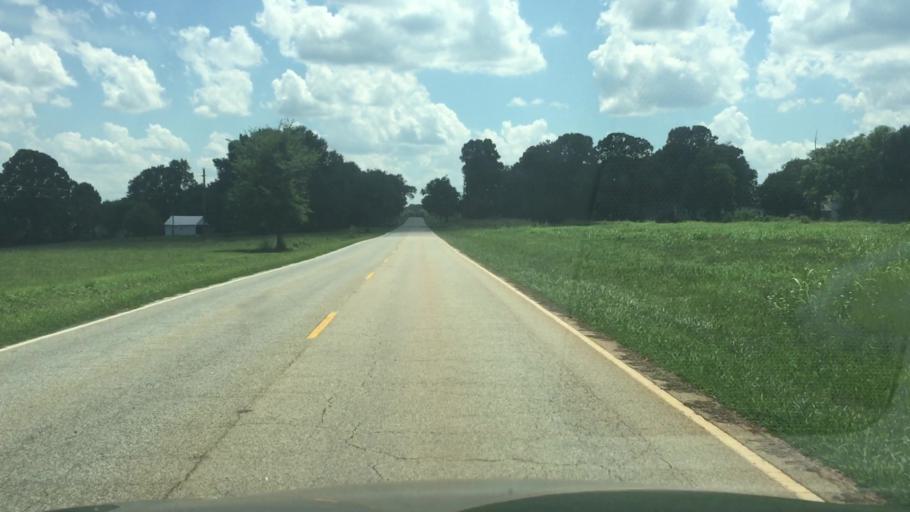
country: US
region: North Carolina
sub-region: Rowan County
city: China Grove
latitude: 35.6339
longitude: -80.6422
